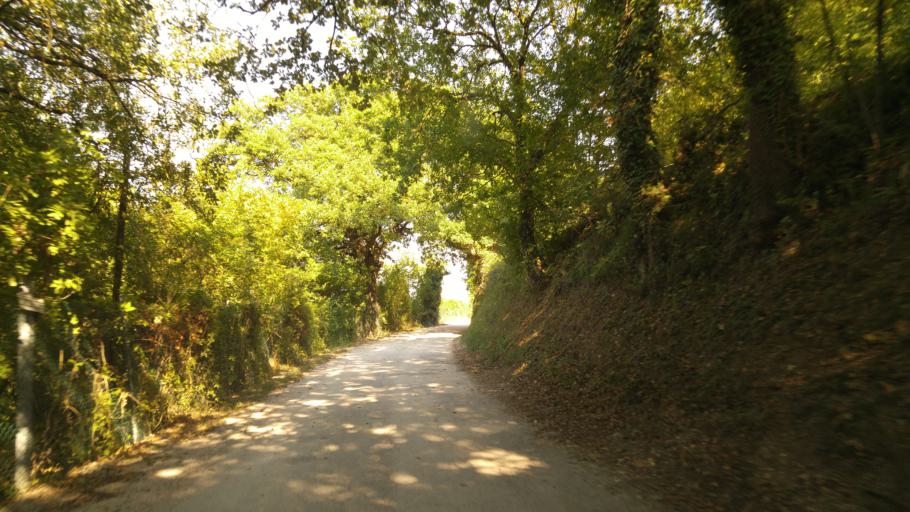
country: IT
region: The Marches
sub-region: Provincia di Pesaro e Urbino
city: Fossombrone
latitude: 43.6834
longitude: 12.7806
